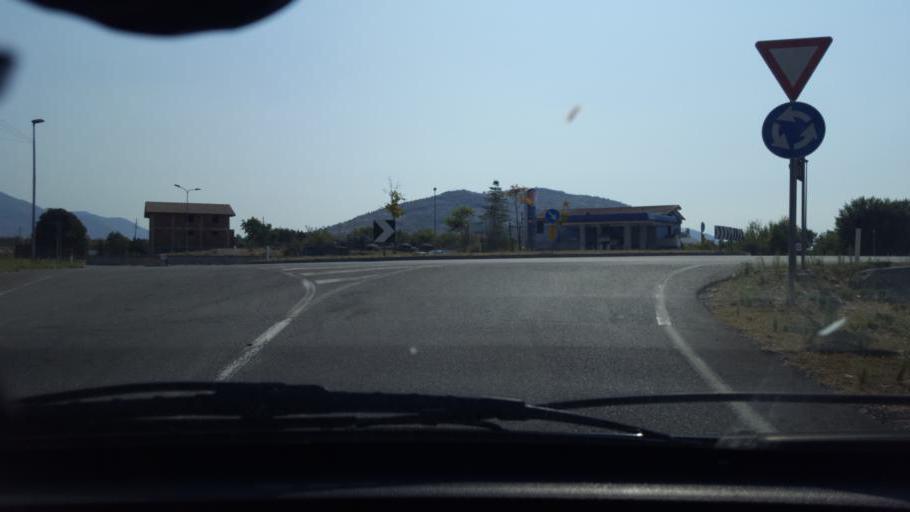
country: AL
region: Shkoder
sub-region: Rrethi i Malesia e Madhe
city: Hot
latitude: 42.3361
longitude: 19.4356
